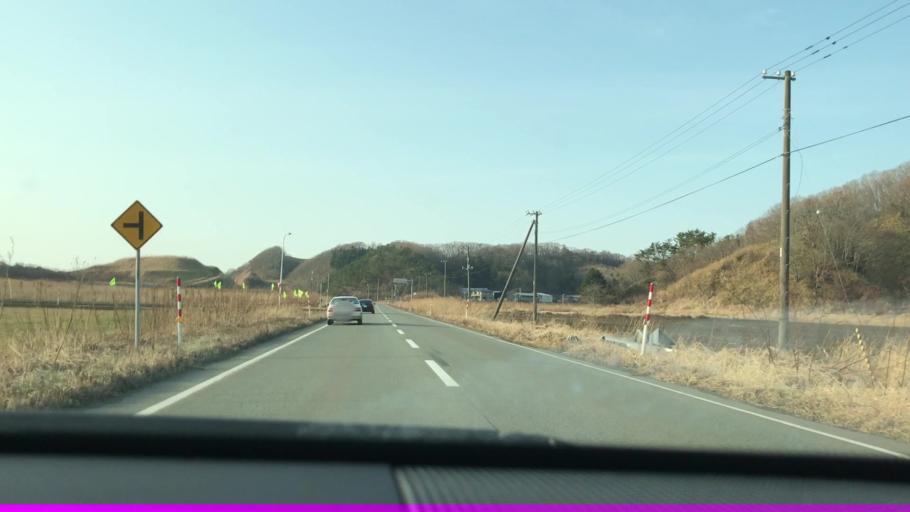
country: JP
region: Hokkaido
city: Shizunai-furukawacho
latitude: 42.2295
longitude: 142.6143
